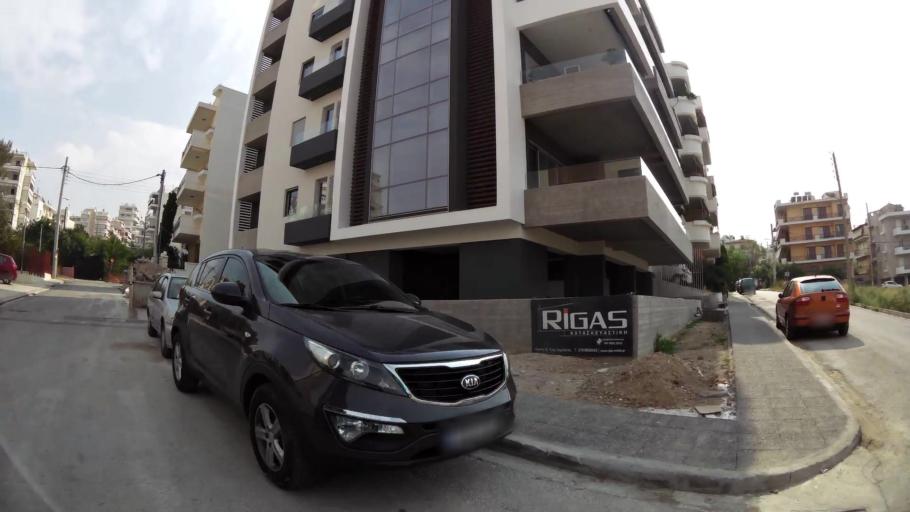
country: GR
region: Attica
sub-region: Nomarchia Athinas
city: Agios Dimitrios
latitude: 37.9261
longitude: 23.7278
